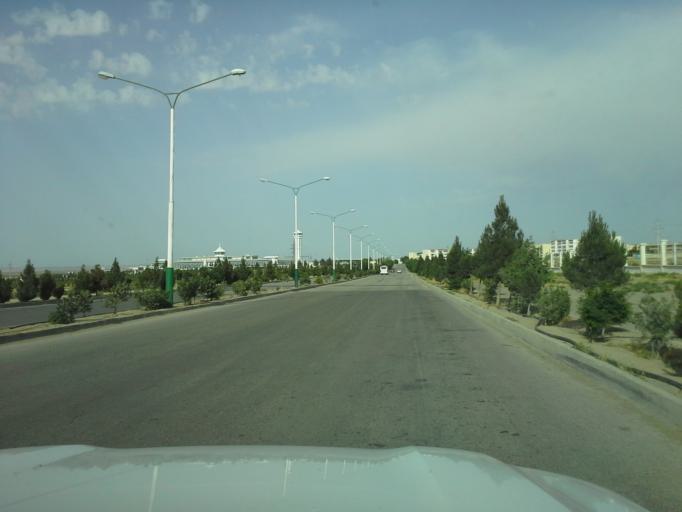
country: TM
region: Balkan
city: Turkmenbasy
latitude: 40.0392
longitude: 52.9818
